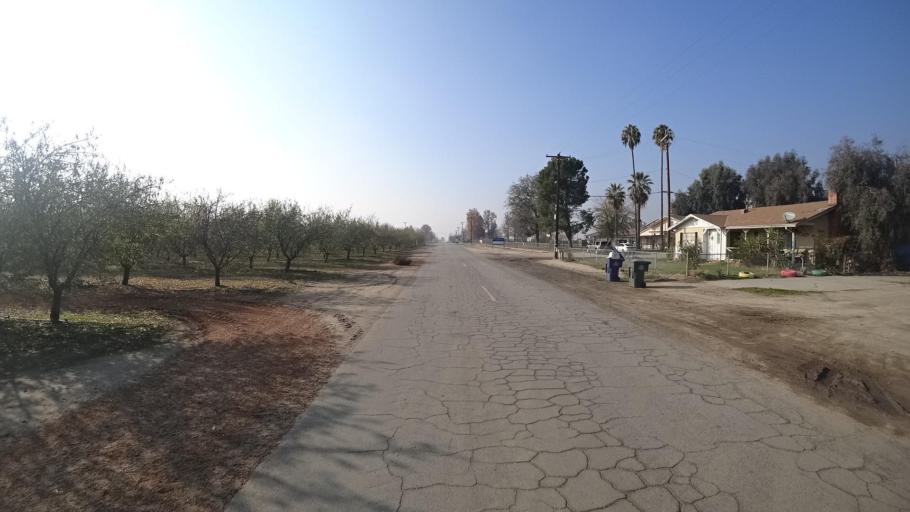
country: US
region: California
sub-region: Kern County
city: Greenfield
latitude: 35.2231
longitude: -119.0161
